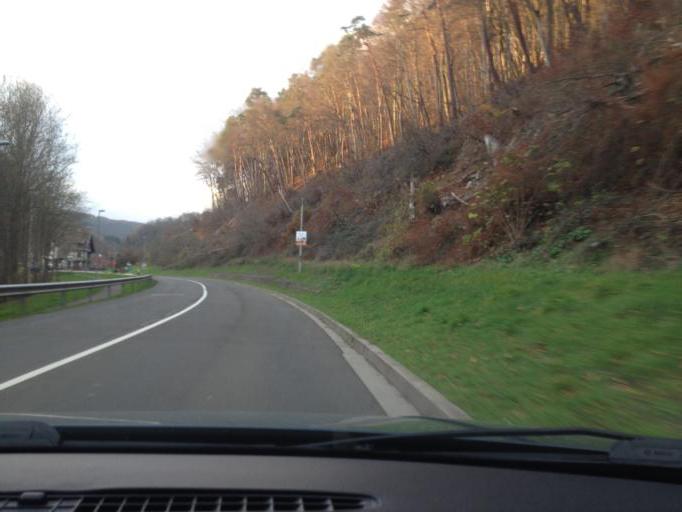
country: DE
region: Rheinland-Pfalz
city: Weidenthal
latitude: 49.4145
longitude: 8.0047
